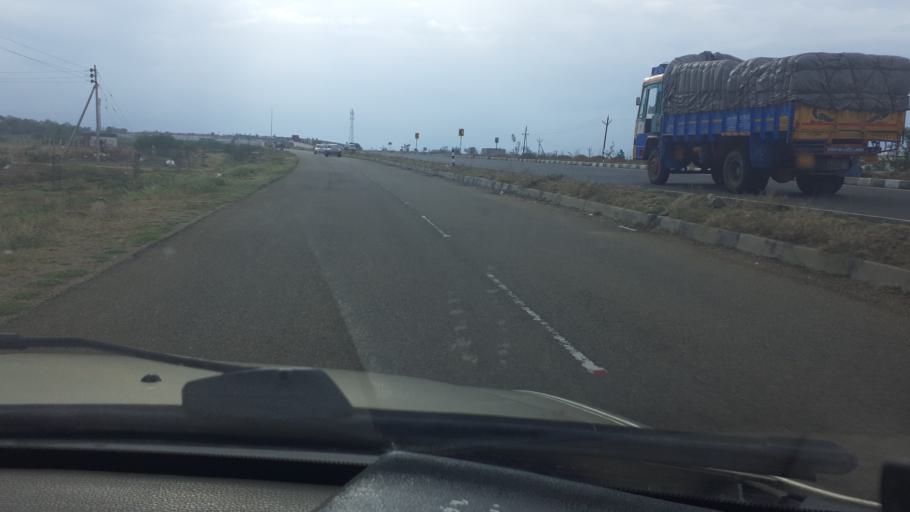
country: IN
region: Tamil Nadu
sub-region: Tirunelveli Kattabo
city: Tirunelveli
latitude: 8.6612
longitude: 77.7195
